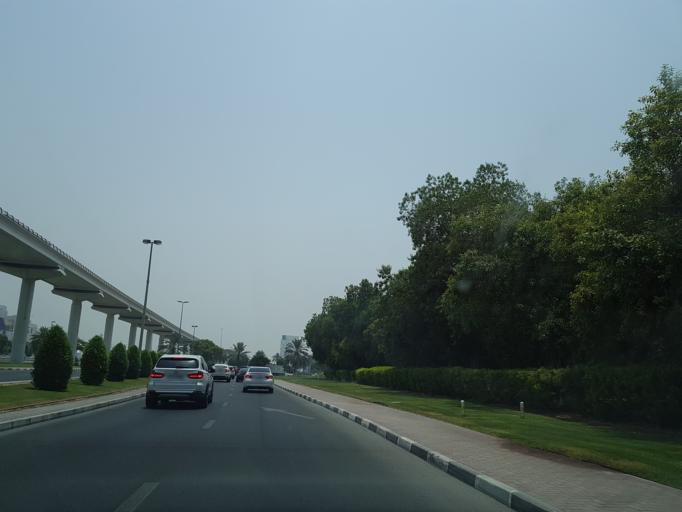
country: AE
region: Ash Shariqah
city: Sharjah
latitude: 25.2296
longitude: 55.3292
